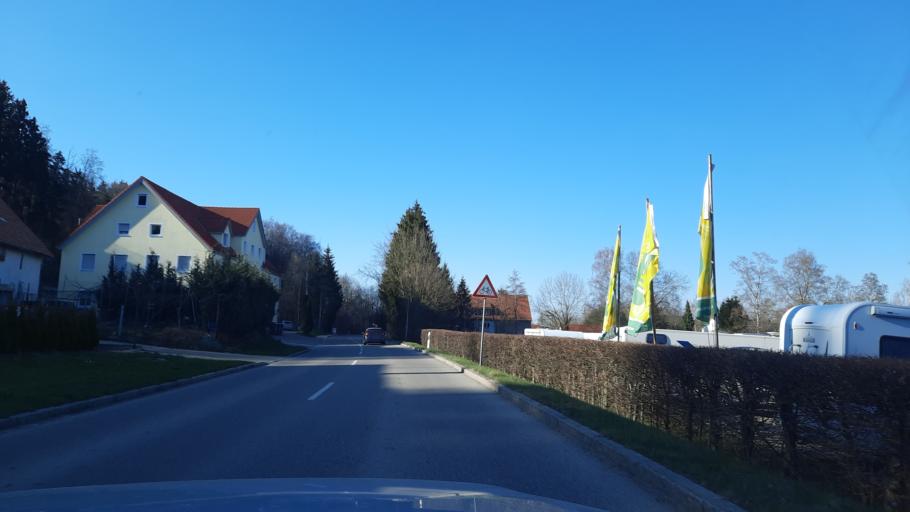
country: DE
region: Bavaria
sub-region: Swabia
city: Memmingen
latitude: 47.9554
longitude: 10.1836
